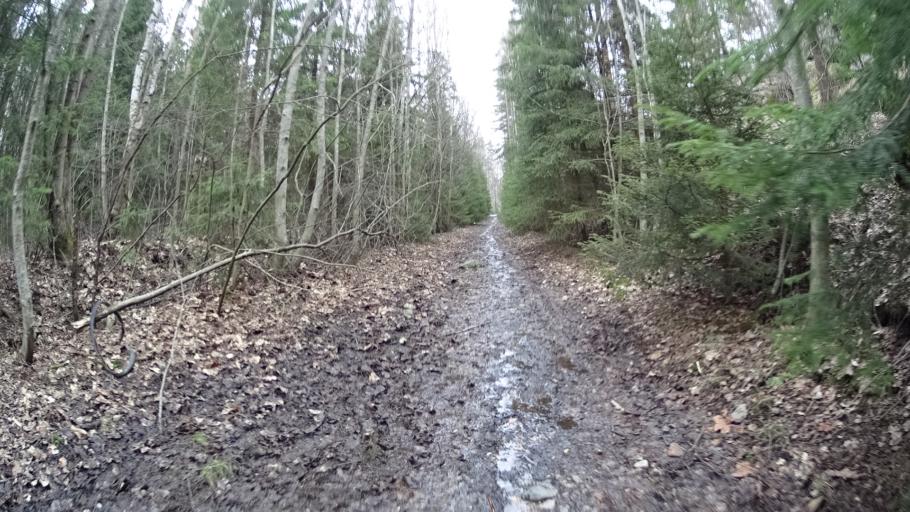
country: FI
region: Uusimaa
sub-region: Helsinki
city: Kilo
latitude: 60.2834
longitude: 24.8037
